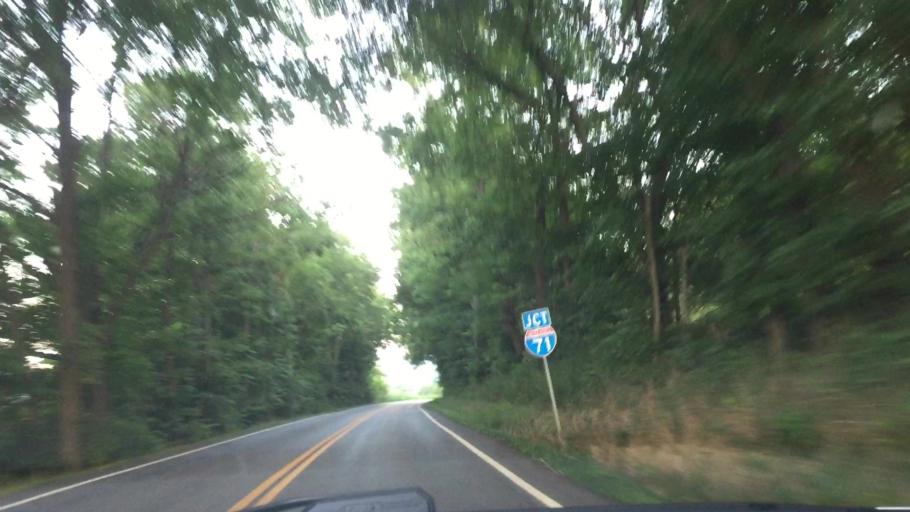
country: US
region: Kentucky
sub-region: Carroll County
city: Carrollton
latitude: 38.6377
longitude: -85.1405
